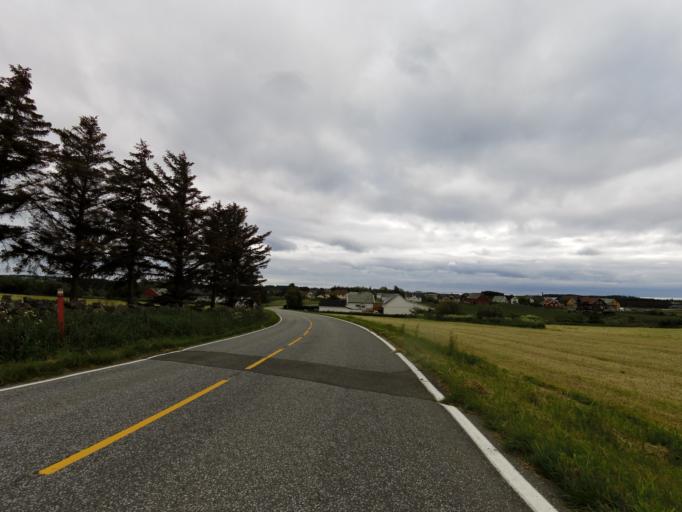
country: NO
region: Vest-Agder
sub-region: Farsund
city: Vestbygd
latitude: 58.1232
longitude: 6.6038
